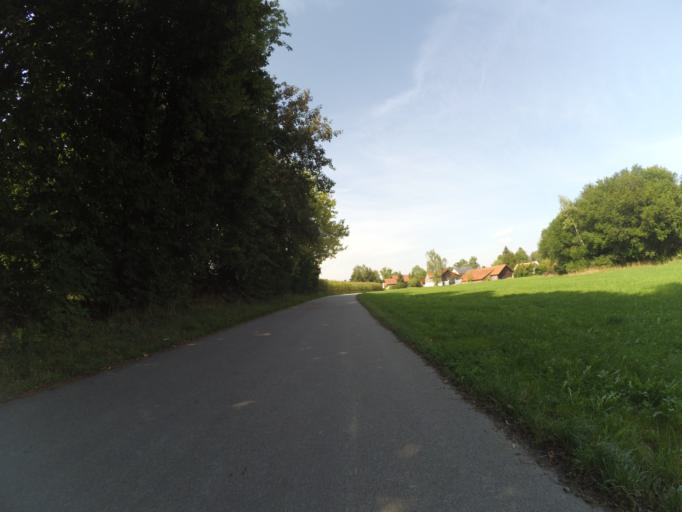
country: DE
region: Bavaria
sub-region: Swabia
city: Lamerdingen
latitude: 48.0807
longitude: 10.7675
